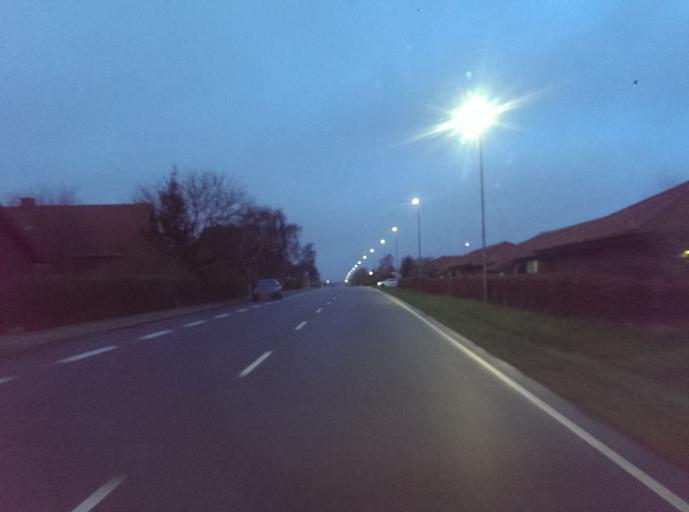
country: DK
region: South Denmark
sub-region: Esbjerg Kommune
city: Tjaereborg
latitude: 55.4984
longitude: 8.5312
